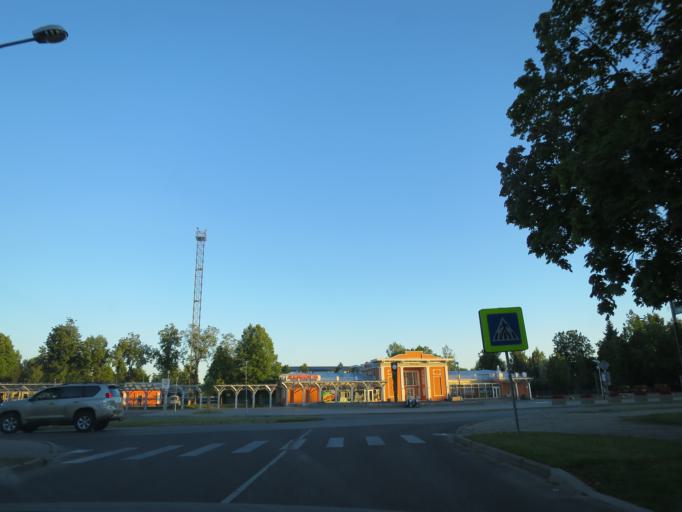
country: LV
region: Sigulda
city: Sigulda
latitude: 57.1542
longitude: 24.8543
